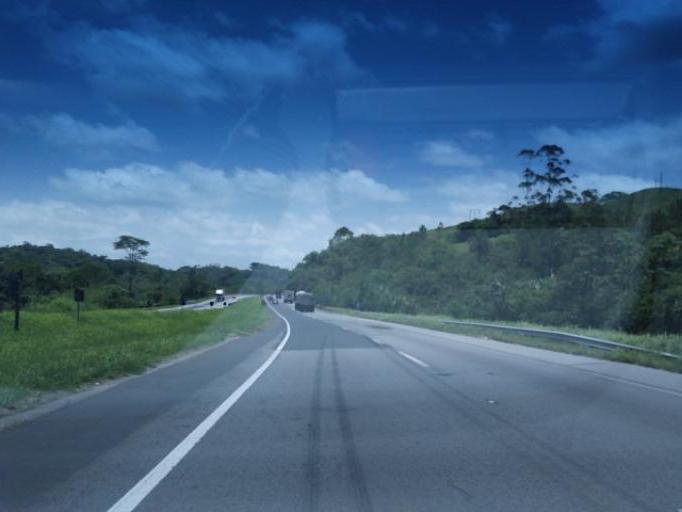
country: BR
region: Sao Paulo
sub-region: Juquia
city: Juquia
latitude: -24.3640
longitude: -47.6919
